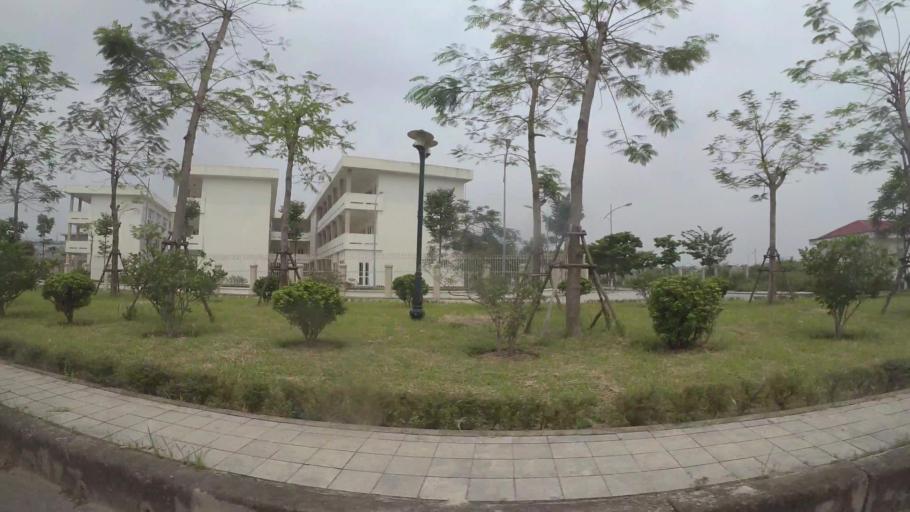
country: VN
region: Ha Noi
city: Ha Dong
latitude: 20.9766
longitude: 105.7536
